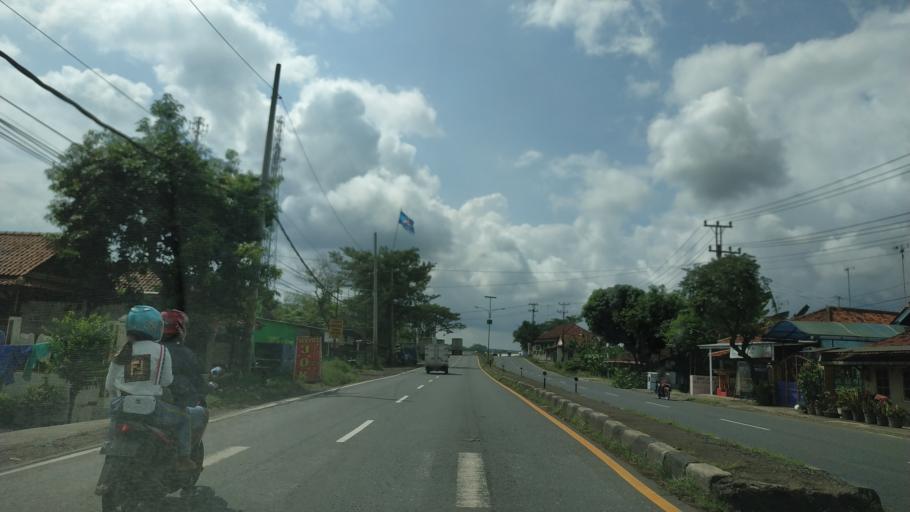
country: ID
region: Central Java
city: Pekalongan
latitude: -6.9523
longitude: 109.8050
